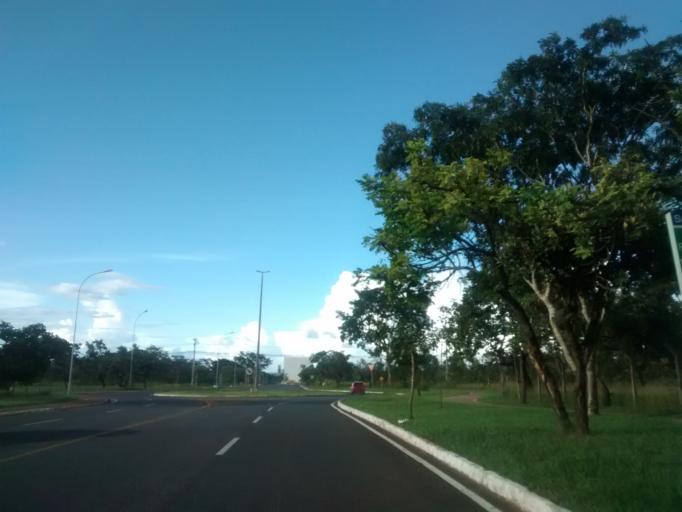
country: BR
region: Federal District
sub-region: Brasilia
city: Brasilia
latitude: -15.7848
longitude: -47.9255
